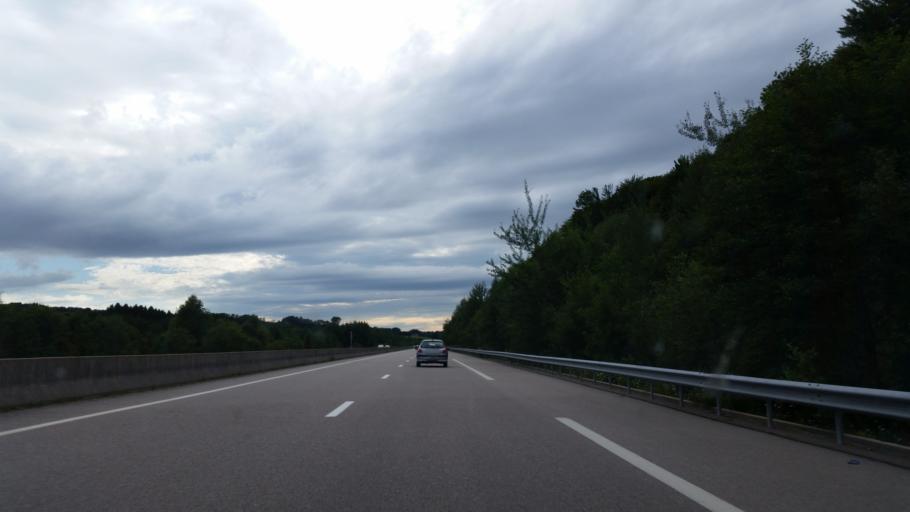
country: FR
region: Lorraine
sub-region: Departement des Vosges
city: Remiremont
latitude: 47.9902
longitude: 6.5295
